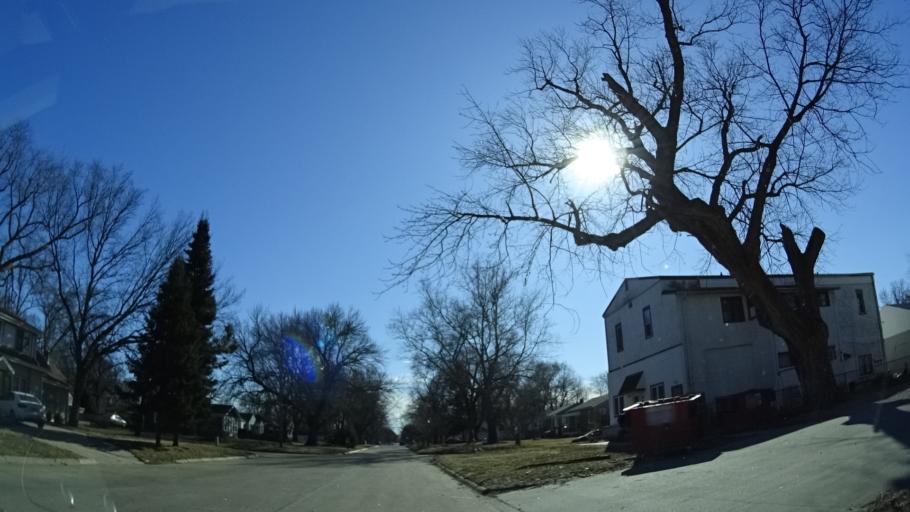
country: US
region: Nebraska
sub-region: Sarpy County
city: Bellevue
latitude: 41.1411
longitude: -95.8909
